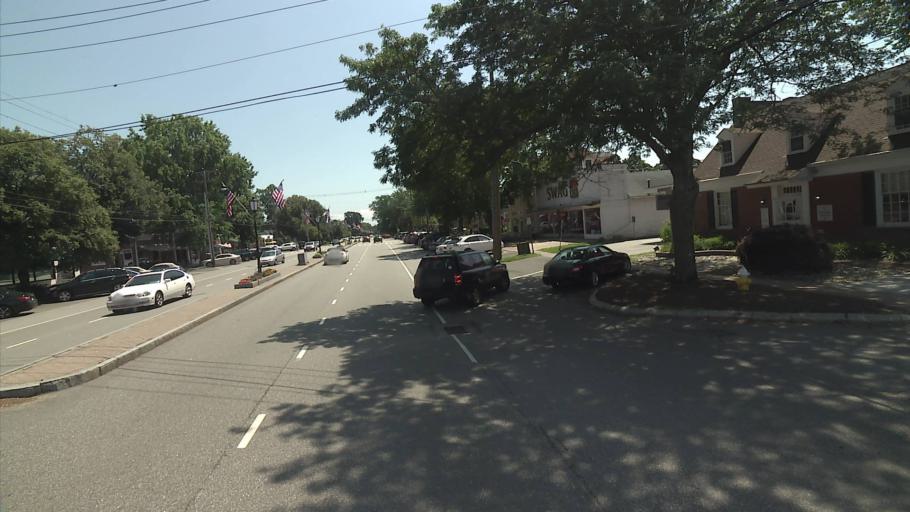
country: US
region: Connecticut
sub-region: Middlesex County
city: Old Saybrook
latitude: 41.2938
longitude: -72.3766
